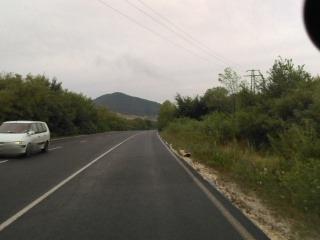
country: BG
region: Plovdiv
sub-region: Obshtina Khisarya
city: Khisarya
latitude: 42.5089
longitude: 24.8130
